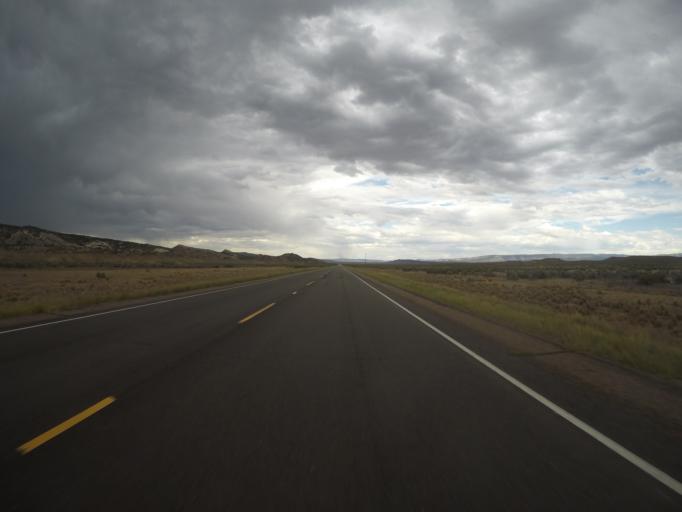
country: US
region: Colorado
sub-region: Rio Blanco County
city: Rangely
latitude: 40.2504
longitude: -108.7755
